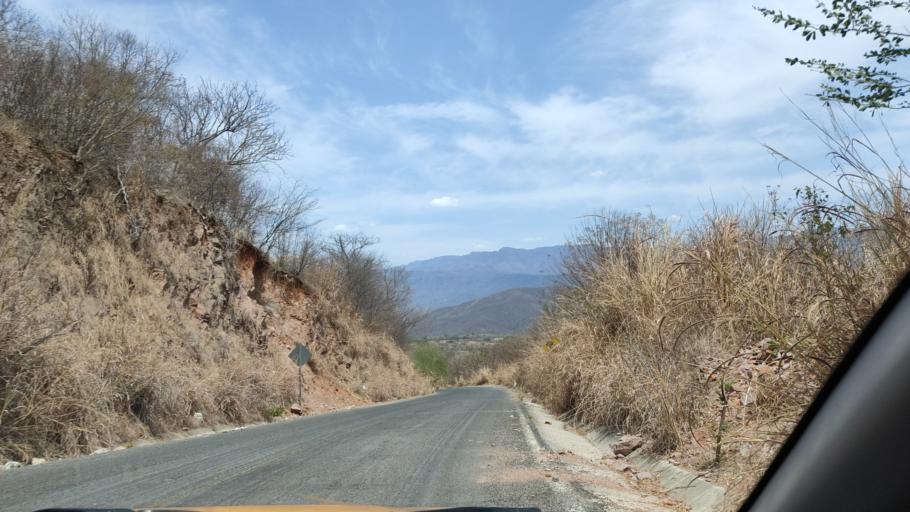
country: MX
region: Nayarit
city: Santa Maria del Oro
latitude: 21.5110
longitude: -104.5974
